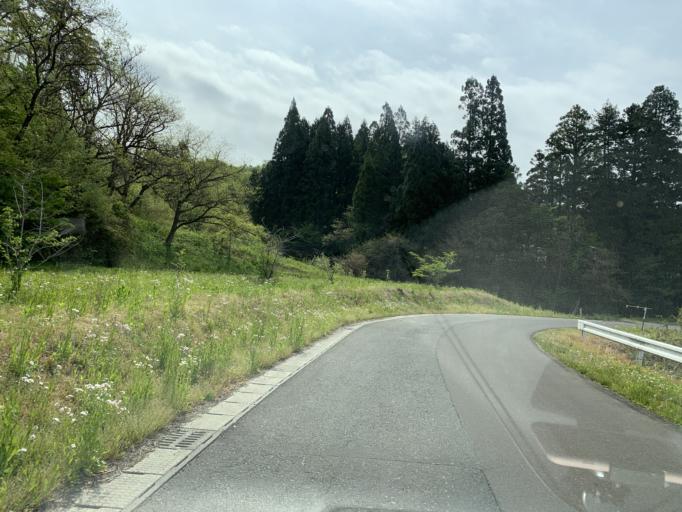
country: JP
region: Iwate
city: Ichinoseki
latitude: 38.8987
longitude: 141.0604
